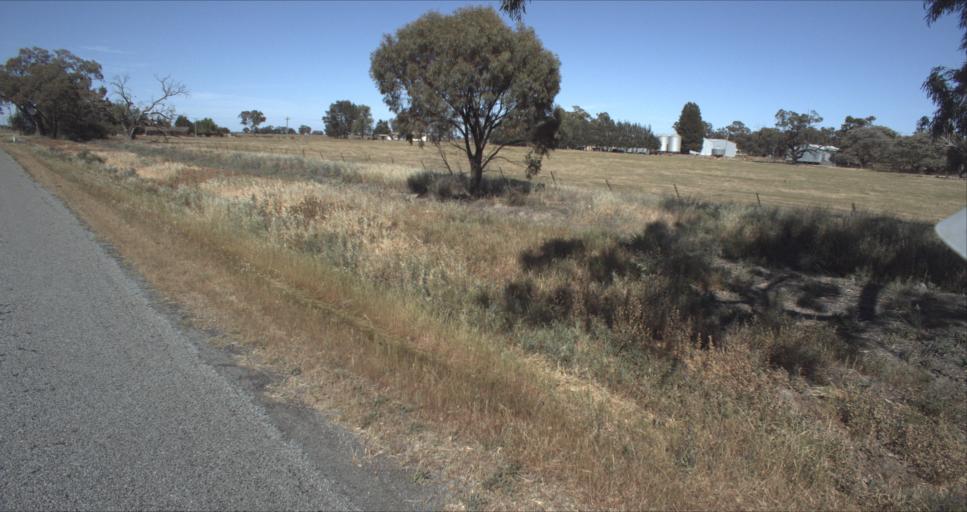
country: AU
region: New South Wales
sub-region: Leeton
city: Leeton
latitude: -34.5420
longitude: 146.3163
